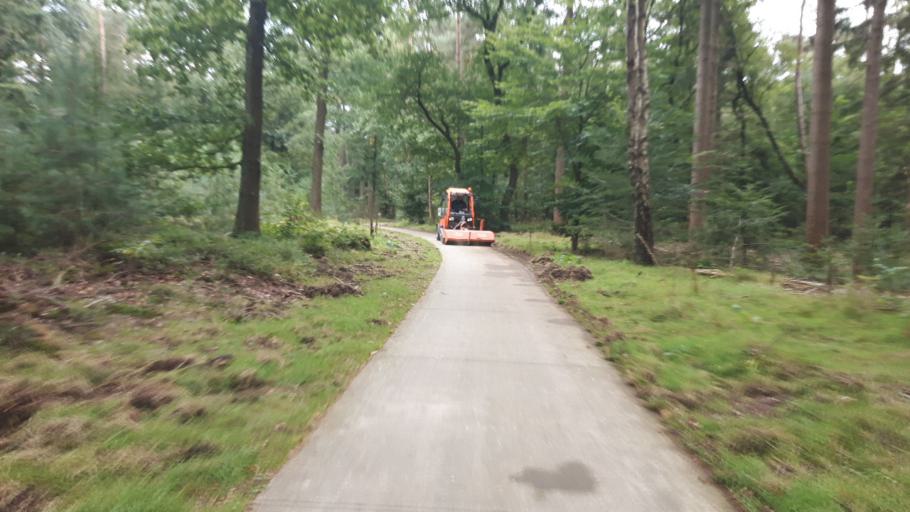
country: NL
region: Gelderland
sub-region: Gemeente Ermelo
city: Ermelo
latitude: 52.2681
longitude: 5.6470
